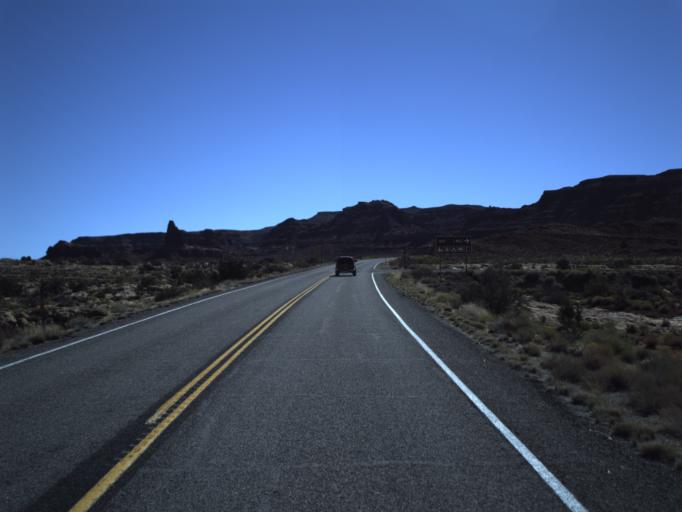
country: US
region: Utah
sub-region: San Juan County
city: Blanding
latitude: 37.8809
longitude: -110.3559
